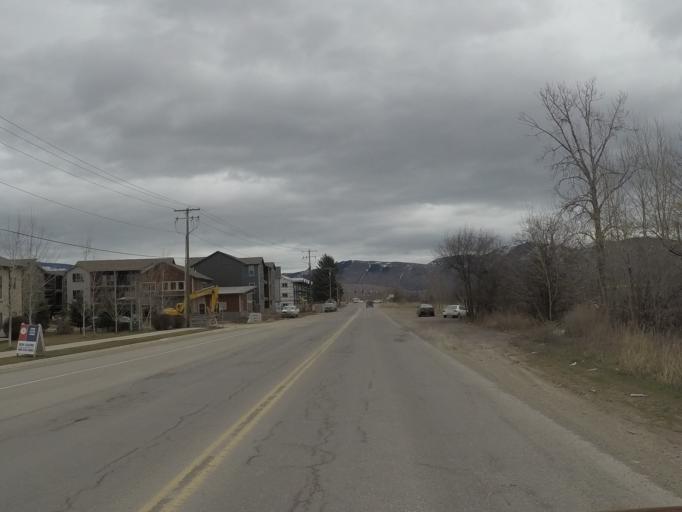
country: US
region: Montana
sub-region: Missoula County
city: Orchard Homes
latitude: 46.8859
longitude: -114.0481
